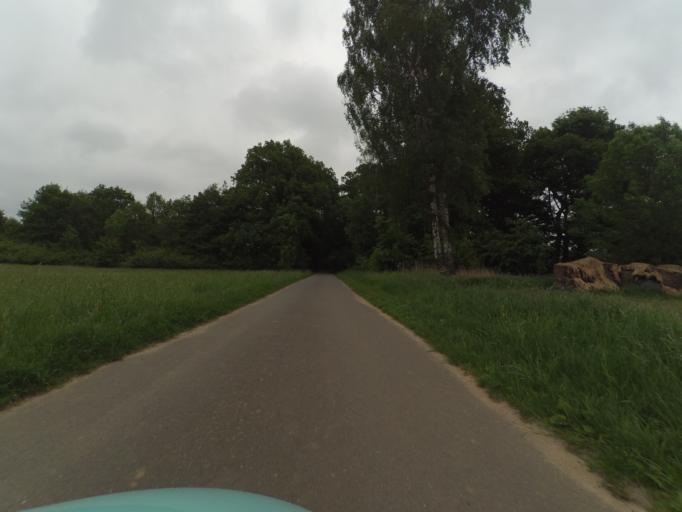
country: DE
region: Lower Saxony
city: Uetze
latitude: 52.4610
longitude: 10.2324
